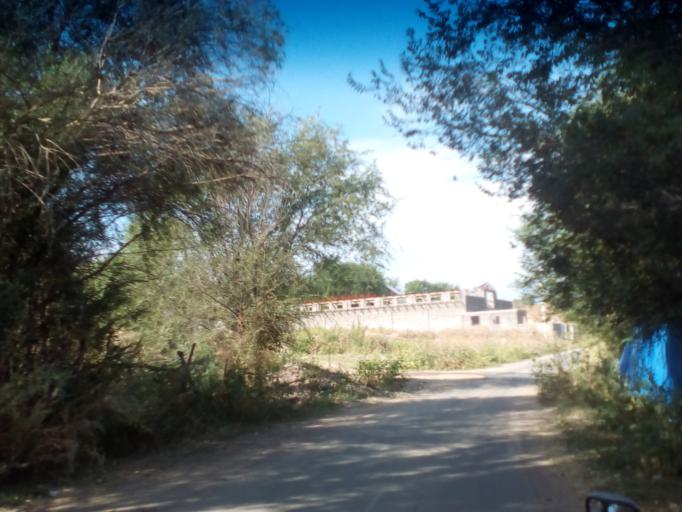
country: KZ
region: Almaty Oblysy
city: Burunday
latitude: 43.1541
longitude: 76.3849
